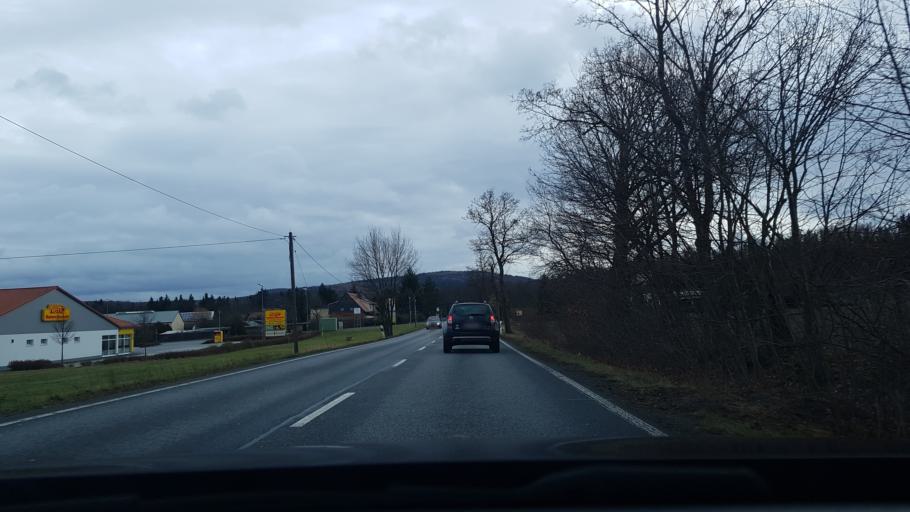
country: DE
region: Saxony
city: Dohma
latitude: 50.8838
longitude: 13.9549
